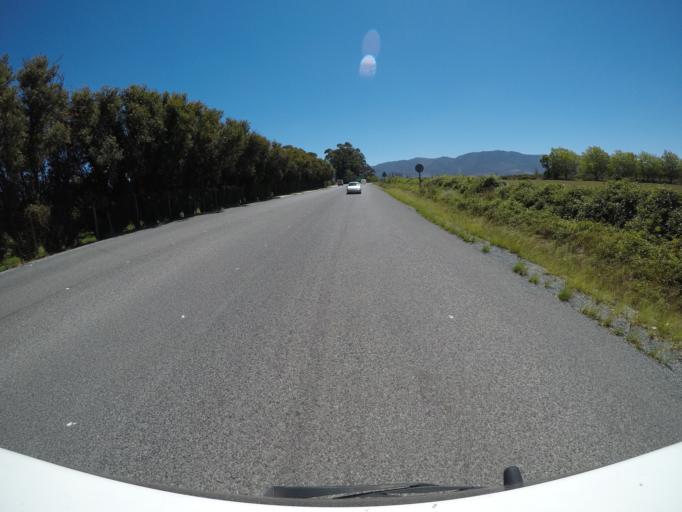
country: ZA
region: Western Cape
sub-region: Overberg District Municipality
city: Grabouw
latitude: -34.1662
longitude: 19.0365
